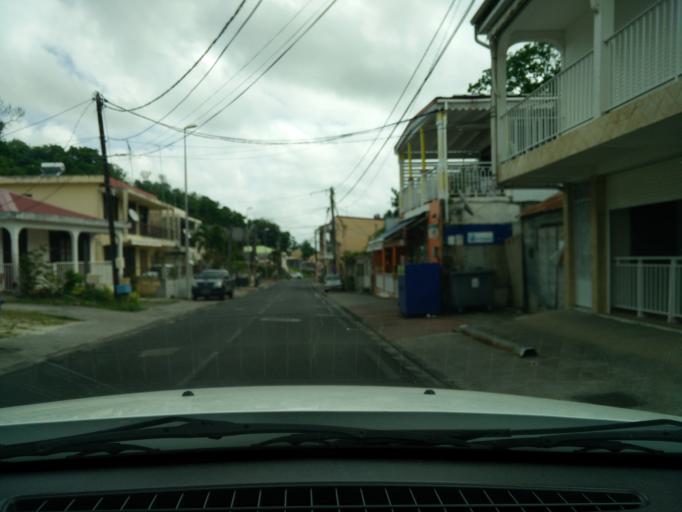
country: GP
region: Guadeloupe
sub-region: Guadeloupe
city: Petit-Canal
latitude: 16.3288
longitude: -61.4590
